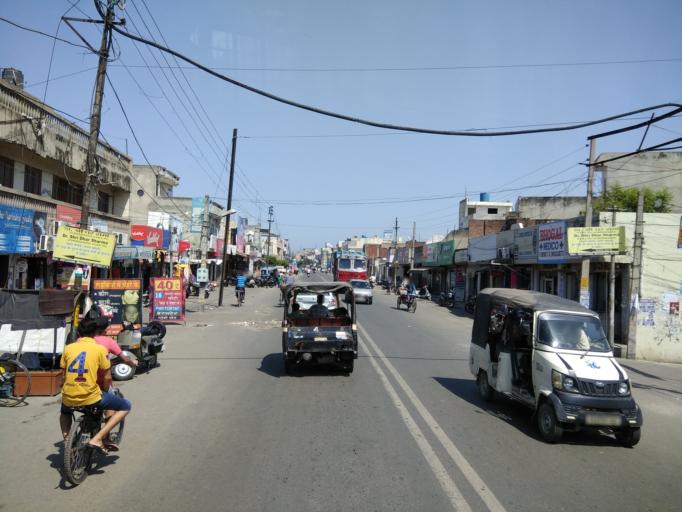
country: IN
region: Punjab
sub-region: Jalandhar
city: Jalandhar
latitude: 31.3416
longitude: 75.5898
